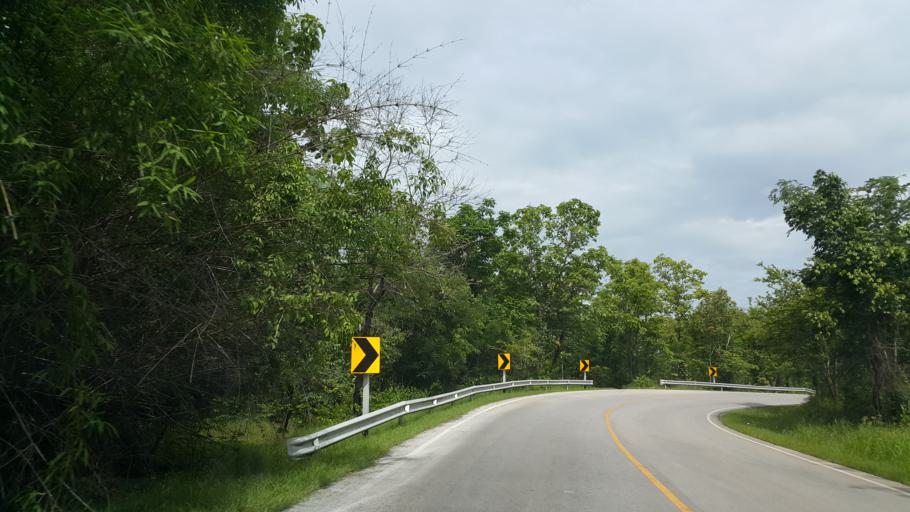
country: TH
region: Lampang
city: Mueang Pan
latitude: 18.7692
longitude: 99.5549
